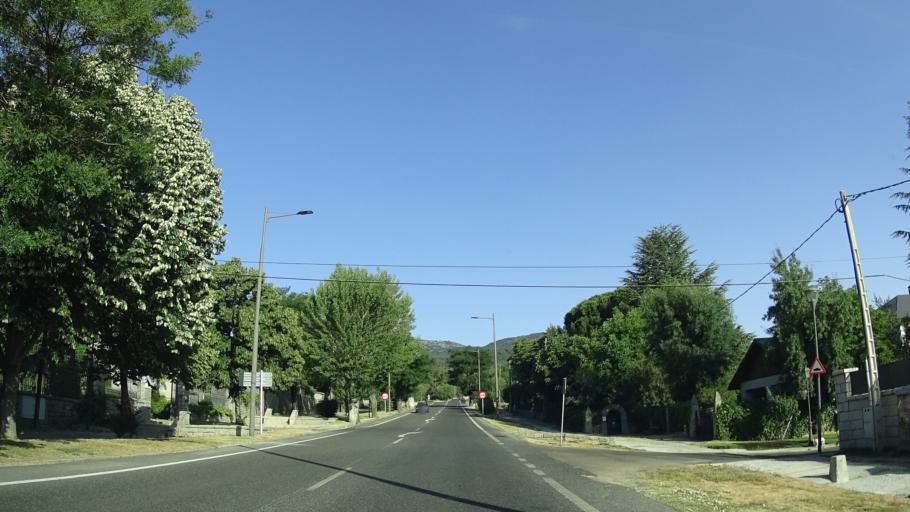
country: ES
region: Madrid
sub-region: Provincia de Madrid
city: Guadarrama
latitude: 40.6770
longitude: -4.1001
